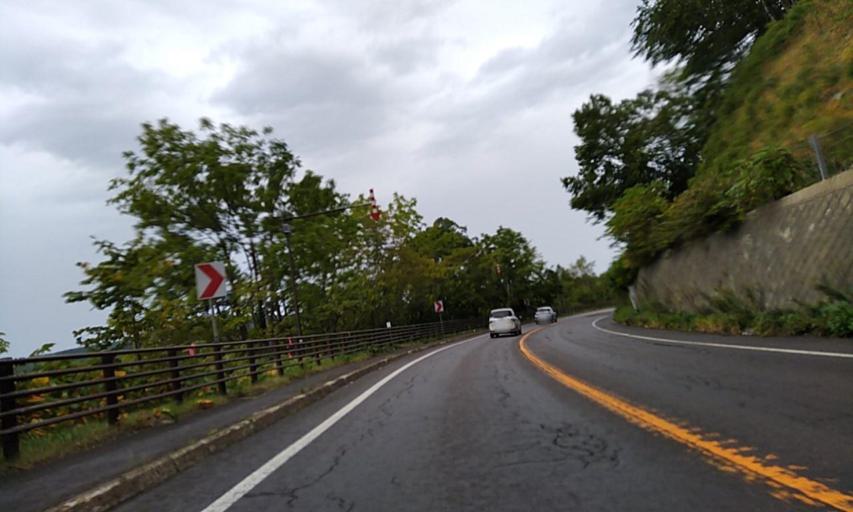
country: JP
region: Hokkaido
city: Abashiri
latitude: 43.9999
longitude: 144.2227
